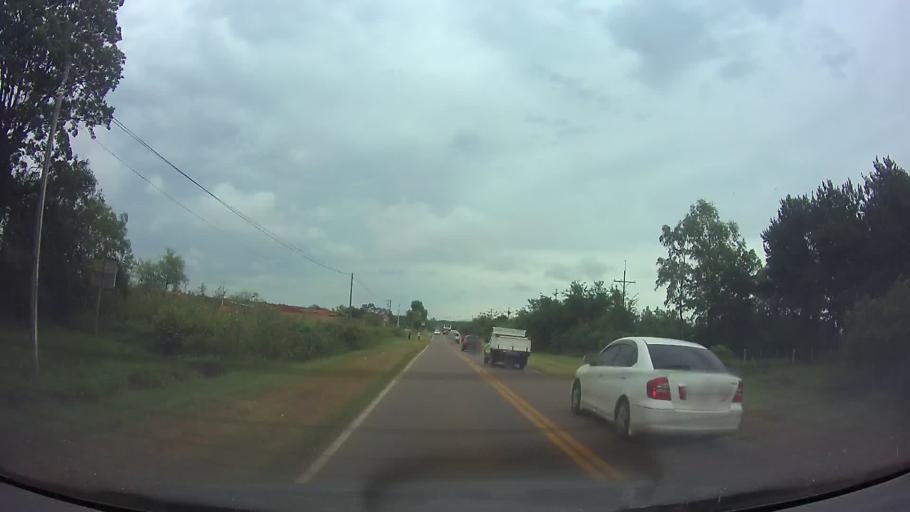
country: PY
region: Paraguari
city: Carapegua
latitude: -25.7802
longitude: -57.2245
